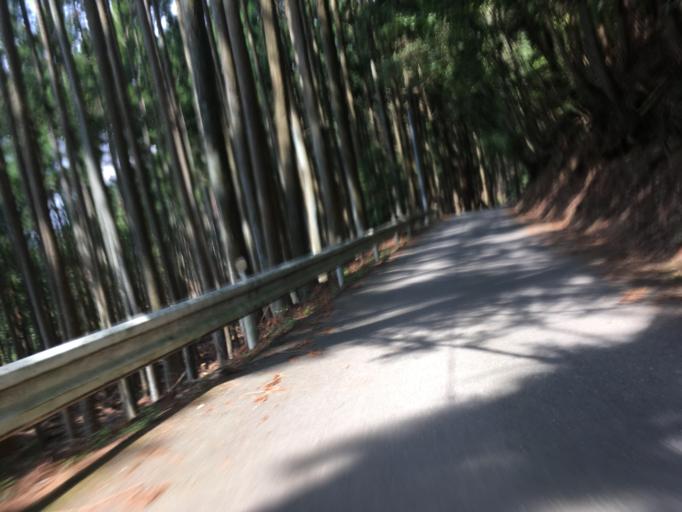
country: JP
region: Kyoto
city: Kameoka
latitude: 35.0675
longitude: 135.6119
